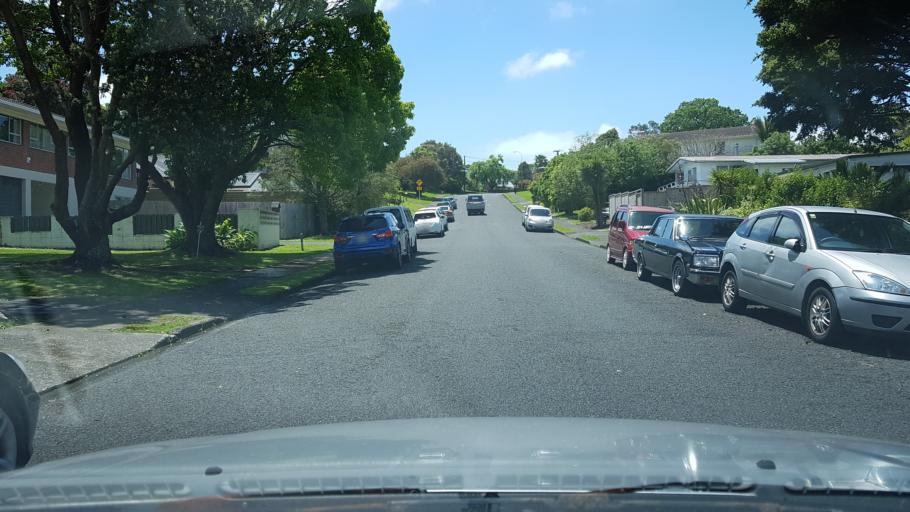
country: NZ
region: Auckland
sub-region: Auckland
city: North Shore
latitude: -36.8014
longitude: 174.7208
